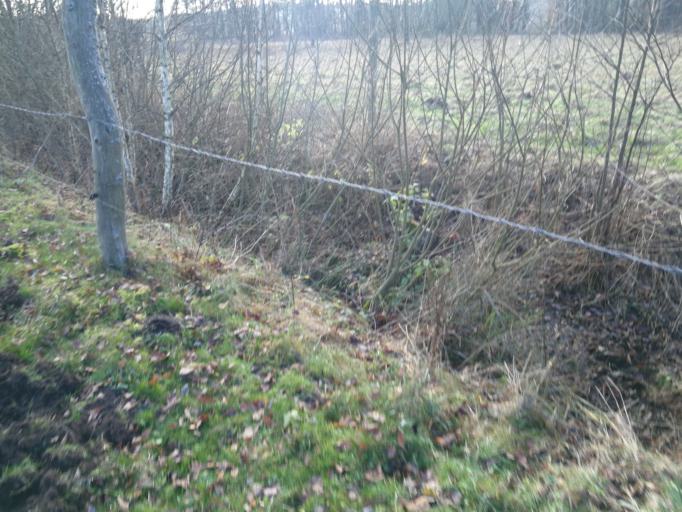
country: PL
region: Warmian-Masurian Voivodeship
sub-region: Powiat dzialdowski
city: Rybno
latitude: 53.4137
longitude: 19.9076
